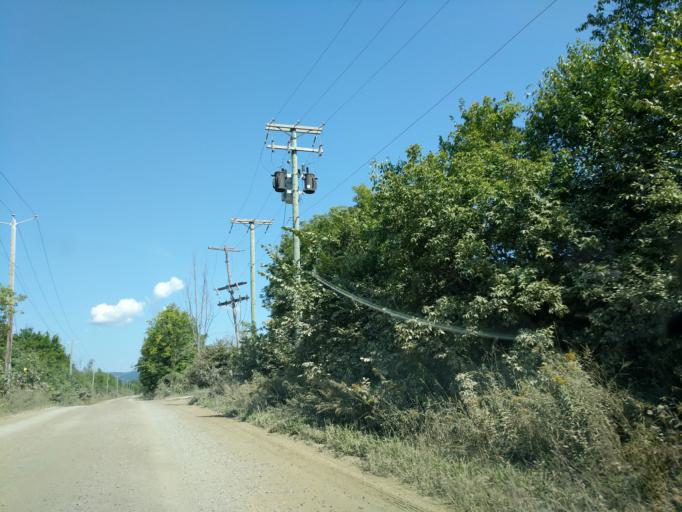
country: CA
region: Ontario
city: Bells Corners
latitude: 45.4410
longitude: -75.9021
